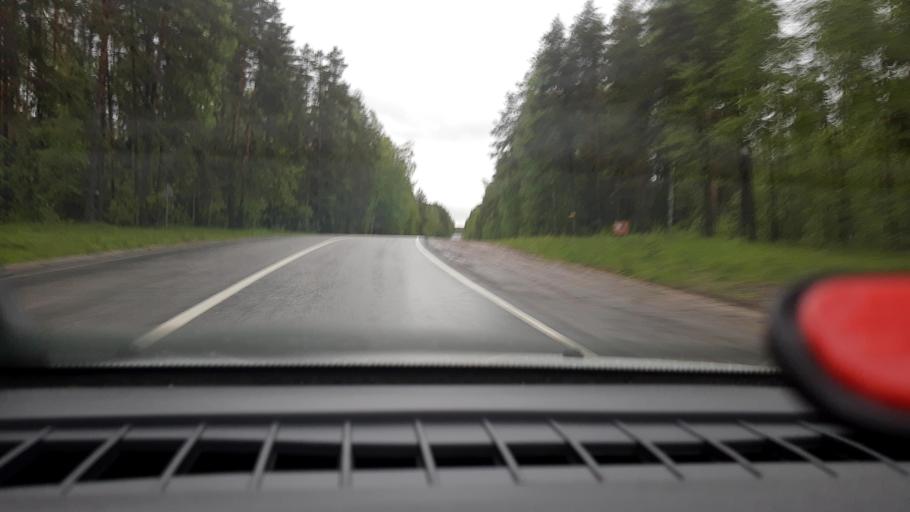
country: RU
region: Nizjnij Novgorod
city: Krasnyye Baki
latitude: 56.9921
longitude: 45.1151
